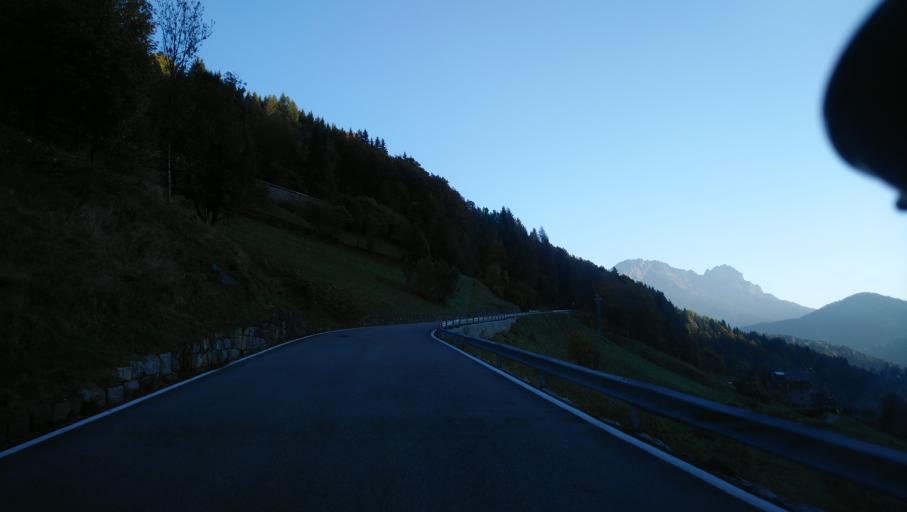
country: IT
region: Veneto
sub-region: Provincia di Belluno
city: Falcade Alto
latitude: 46.3548
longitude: 11.8604
